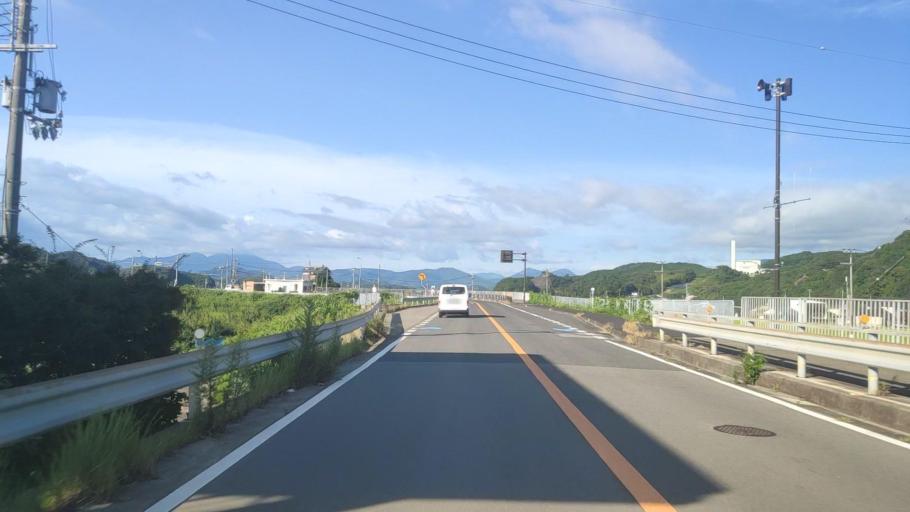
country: JP
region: Wakayama
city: Tanabe
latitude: 33.6782
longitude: 135.4091
